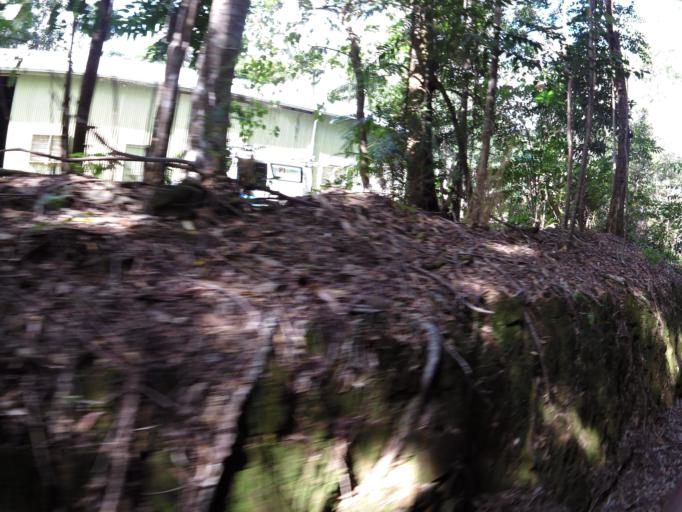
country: AU
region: Queensland
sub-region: Tablelands
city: Kuranda
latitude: -16.8308
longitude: 145.6382
